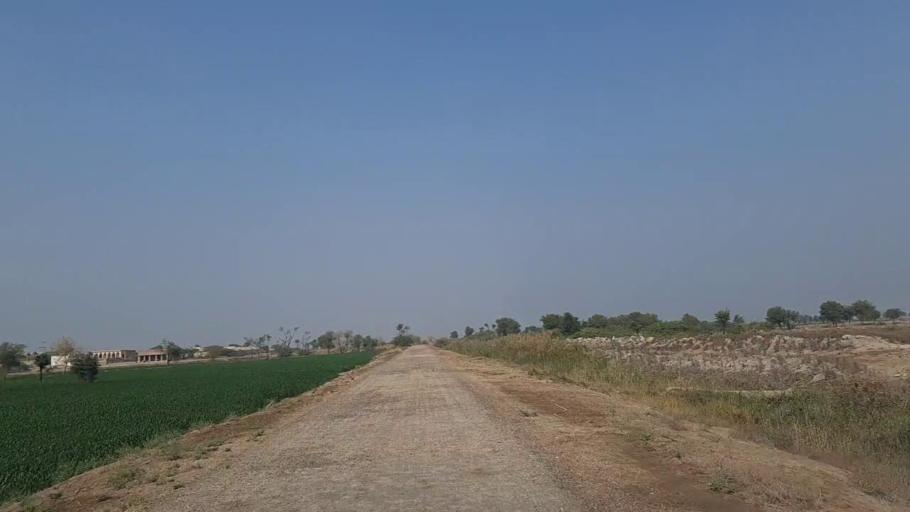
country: PK
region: Sindh
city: Nawabshah
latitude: 26.3676
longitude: 68.4263
